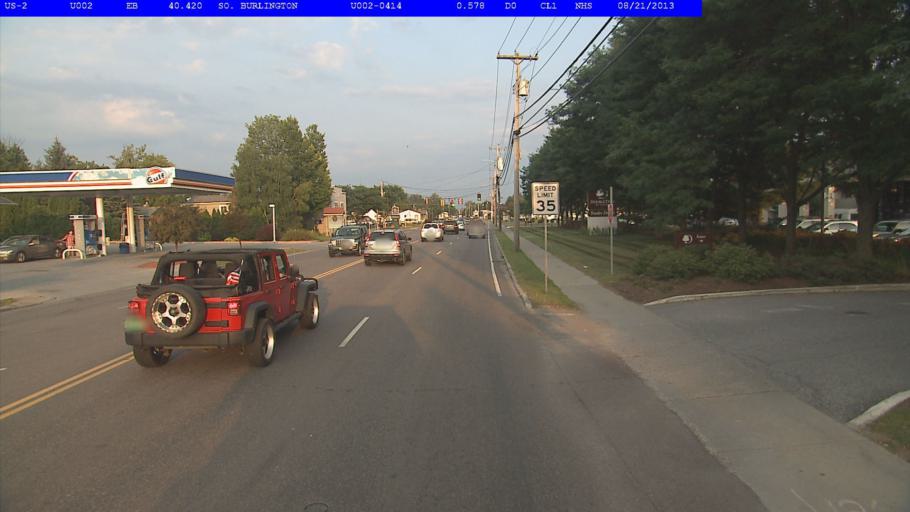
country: US
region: Vermont
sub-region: Chittenden County
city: South Burlington
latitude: 44.4687
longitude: -73.1798
